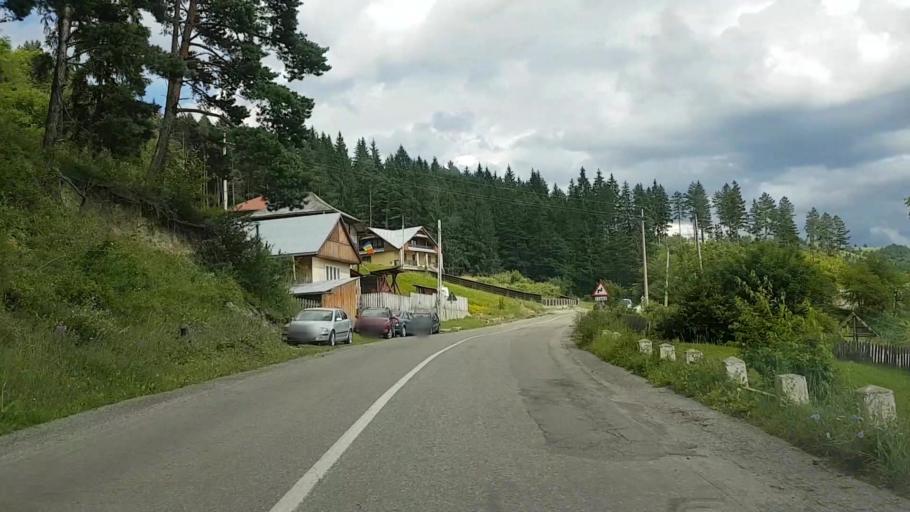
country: RO
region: Neamt
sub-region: Comuna Hangu
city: Hangu
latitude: 47.0098
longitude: 26.0877
